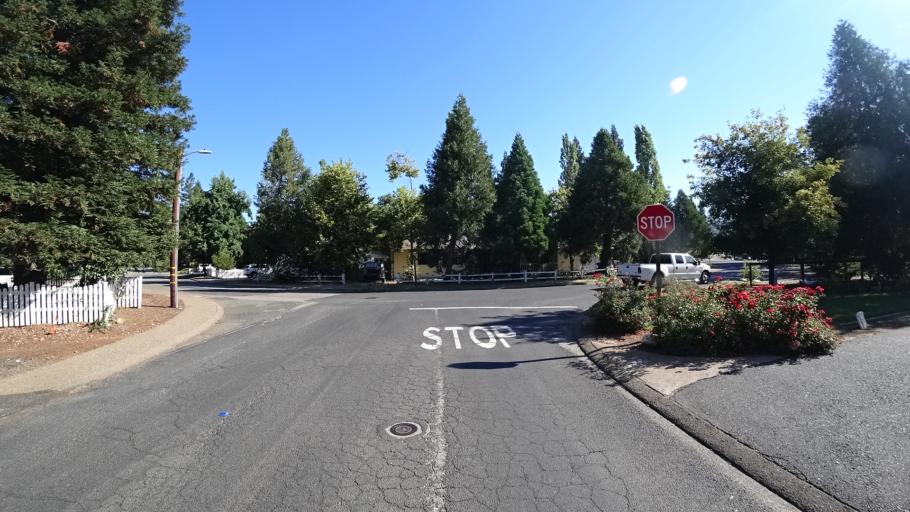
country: US
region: California
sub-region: Calaveras County
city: Murphys
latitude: 38.1406
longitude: -120.4619
